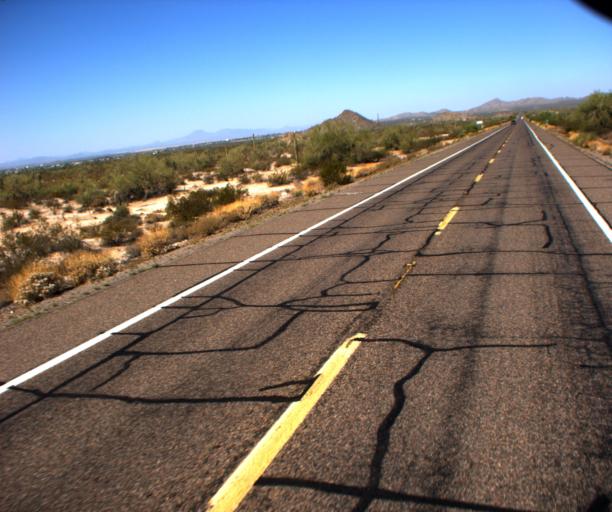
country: US
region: Arizona
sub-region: Pinal County
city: Sacaton
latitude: 33.0056
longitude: -111.7129
